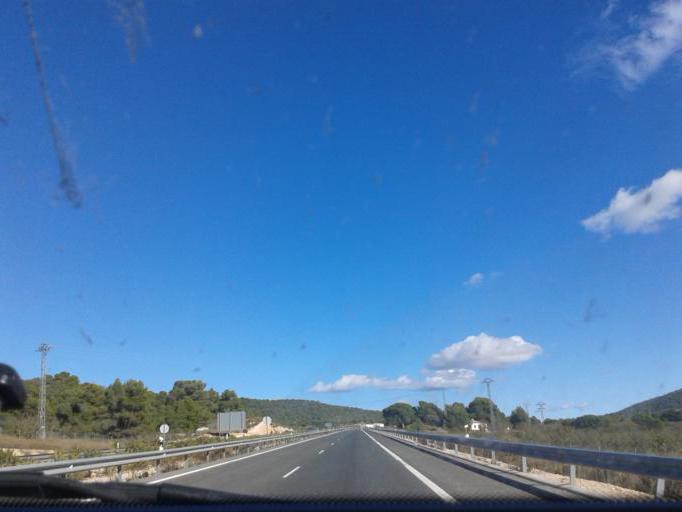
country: ES
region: Valencia
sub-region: Provincia de Alicante
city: Biar
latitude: 38.5835
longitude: -0.7733
